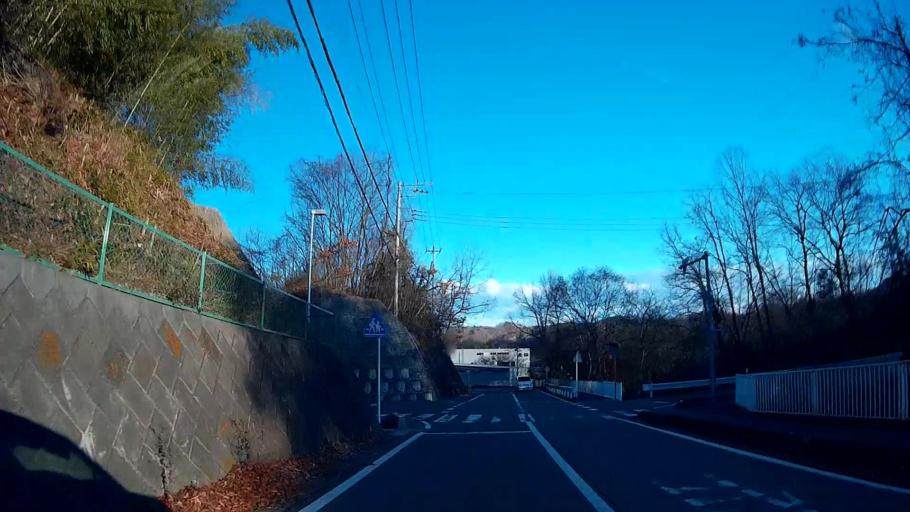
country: JP
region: Saitama
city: Chichibu
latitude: 36.0424
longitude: 139.0251
